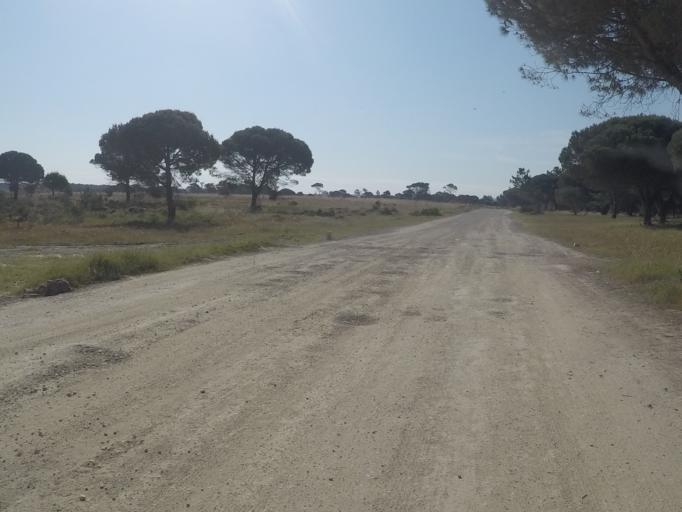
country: PT
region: Setubal
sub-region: Sesimbra
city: Sesimbra
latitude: 38.4925
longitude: -9.1782
